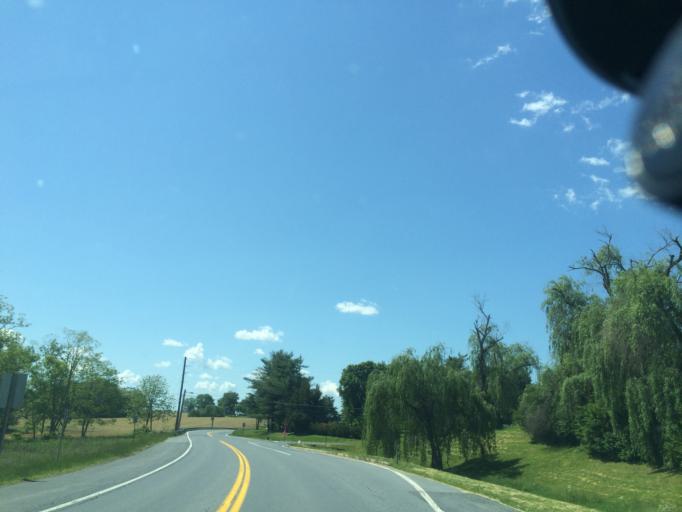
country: US
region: Maryland
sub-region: Carroll County
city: Sykesville
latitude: 39.3949
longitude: -77.0180
